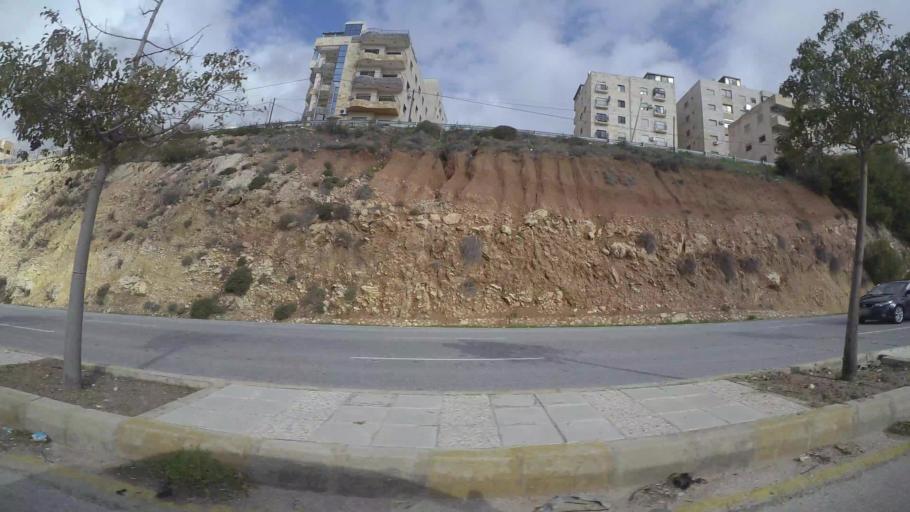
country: JO
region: Amman
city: Al Jubayhah
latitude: 32.0610
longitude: 35.8699
